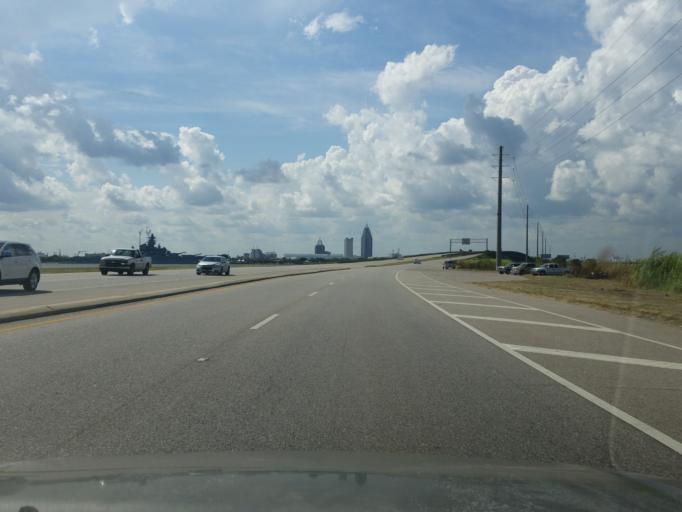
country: US
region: Alabama
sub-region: Mobile County
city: Mobile
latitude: 30.6811
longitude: -88.0038
